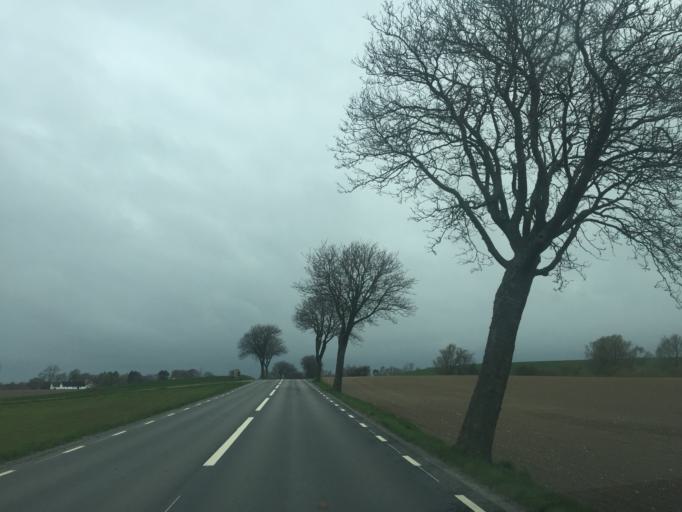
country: SE
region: Skane
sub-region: Skurups Kommun
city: Skivarp
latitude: 55.4204
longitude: 13.6278
